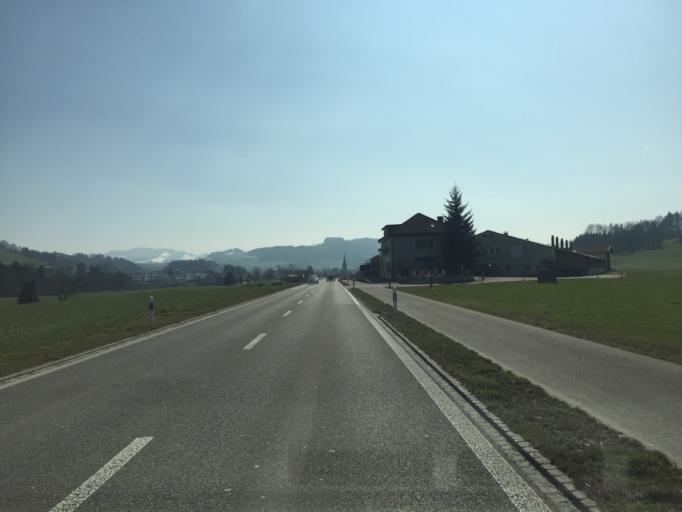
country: CH
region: Saint Gallen
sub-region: Wahlkreis Toggenburg
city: Lutisburg
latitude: 47.4023
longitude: 9.0703
